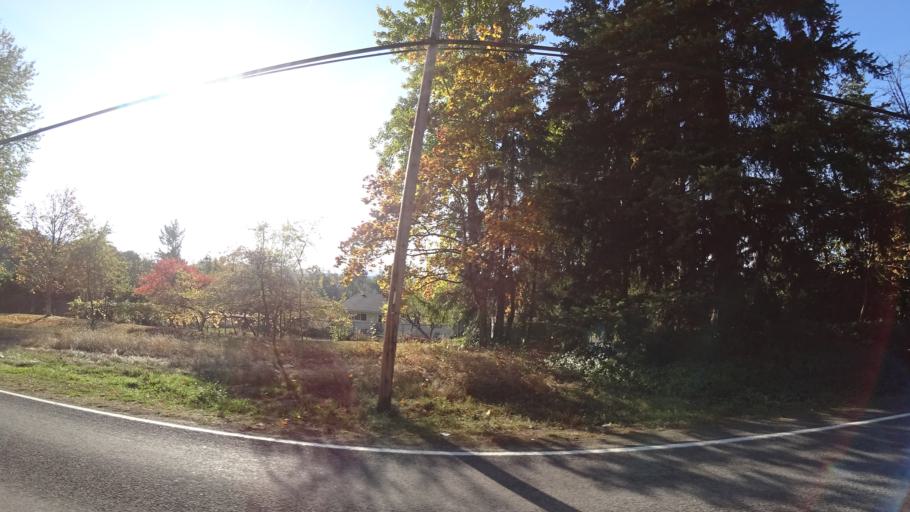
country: US
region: Oregon
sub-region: Multnomah County
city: Gresham
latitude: 45.4757
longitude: -122.4483
